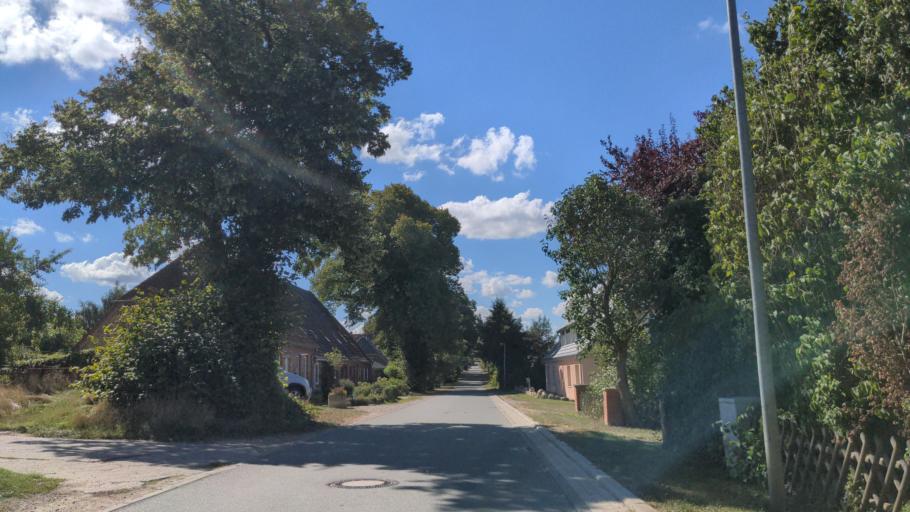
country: DE
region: Mecklenburg-Vorpommern
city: Ostseebad Boltenhagen
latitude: 53.9475
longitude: 11.2271
